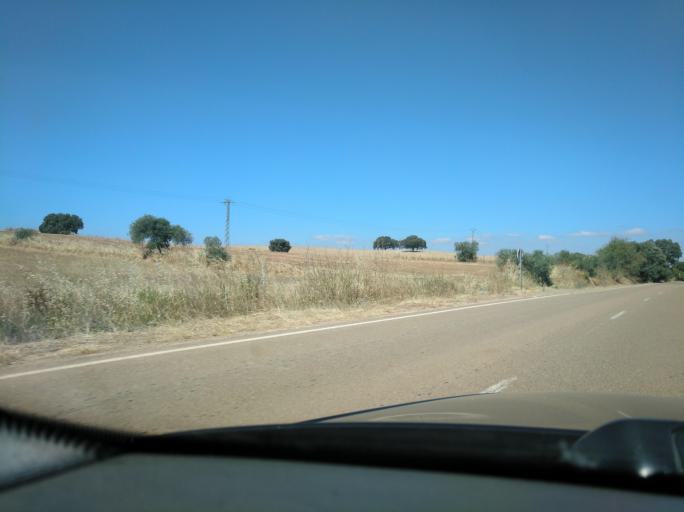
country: ES
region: Extremadura
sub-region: Provincia de Badajoz
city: Olivenza
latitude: 38.6981
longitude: -7.1434
